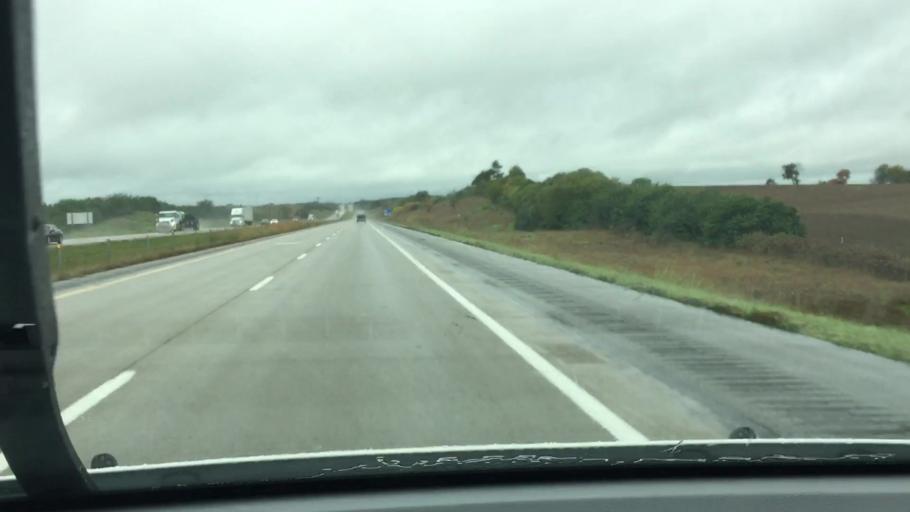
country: US
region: Iowa
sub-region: Jasper County
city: Newton
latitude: 41.6806
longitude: -92.9518
